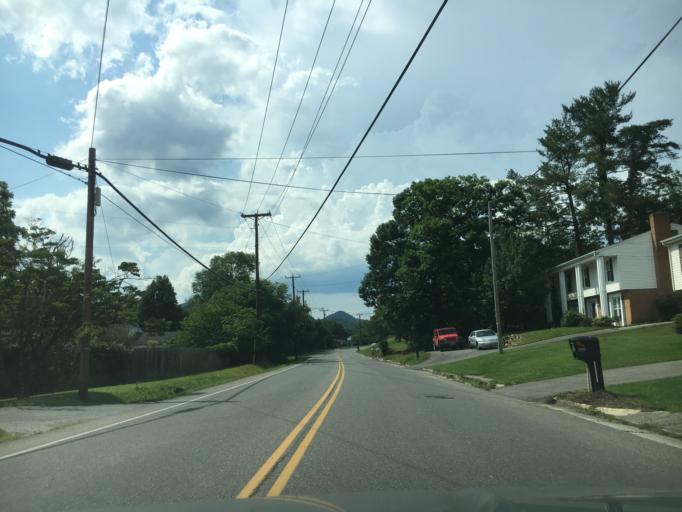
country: US
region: Virginia
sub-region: Roanoke County
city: Cave Spring
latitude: 37.2105
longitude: -80.0120
